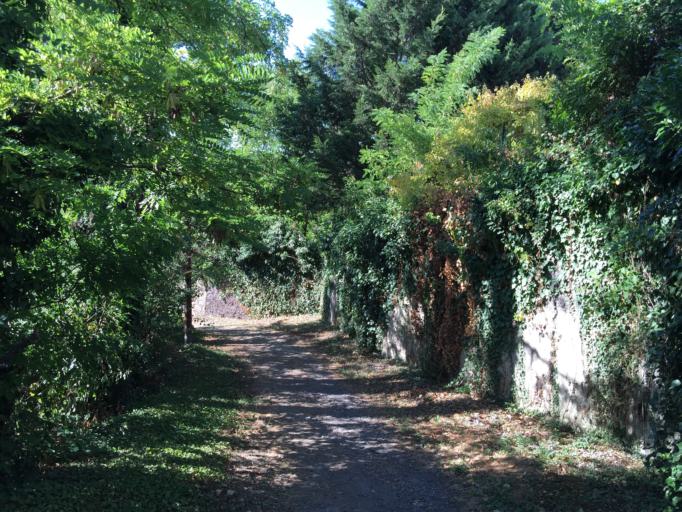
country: FR
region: Rhone-Alpes
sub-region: Departement de la Loire
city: Lorette
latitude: 45.5018
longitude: 4.5661
